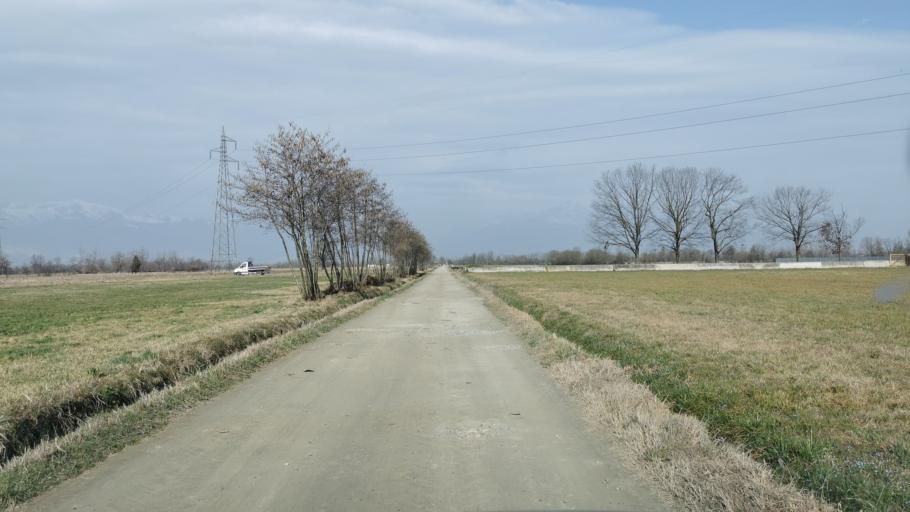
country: IT
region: Piedmont
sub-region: Provincia di Torino
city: Rivarossa
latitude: 45.2726
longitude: 7.7033
